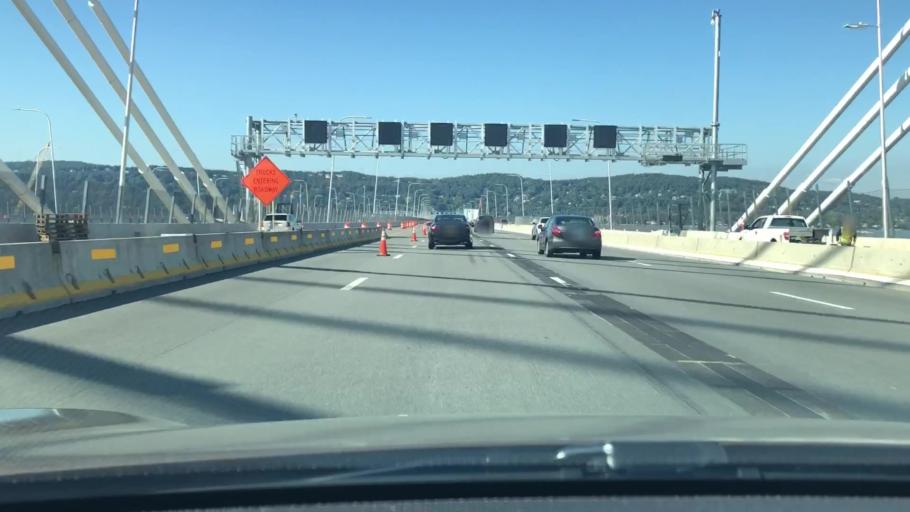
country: US
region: New York
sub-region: Westchester County
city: Tarrytown
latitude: 41.0714
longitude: -73.8845
